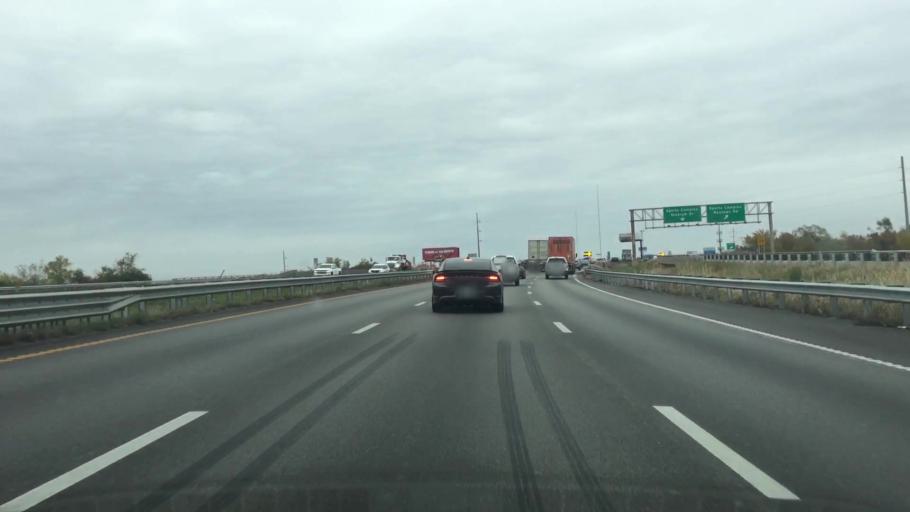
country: US
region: Missouri
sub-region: Jackson County
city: Raytown
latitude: 39.0503
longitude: -94.4990
